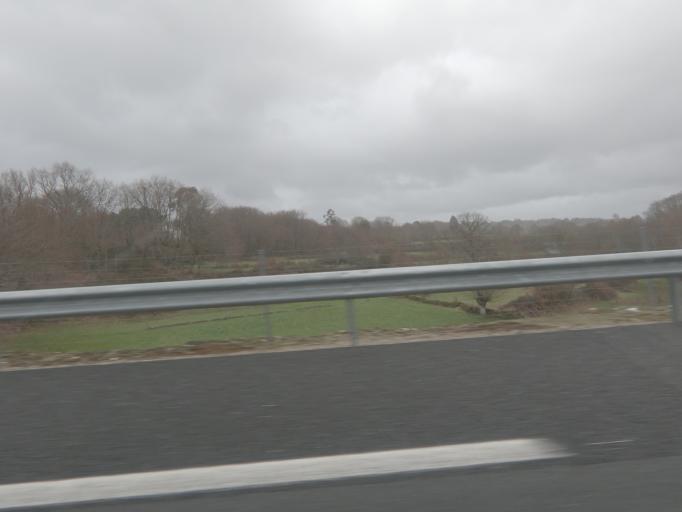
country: ES
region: Galicia
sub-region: Provincia de Pontevedra
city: Silleda
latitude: 42.6987
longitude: -8.2042
